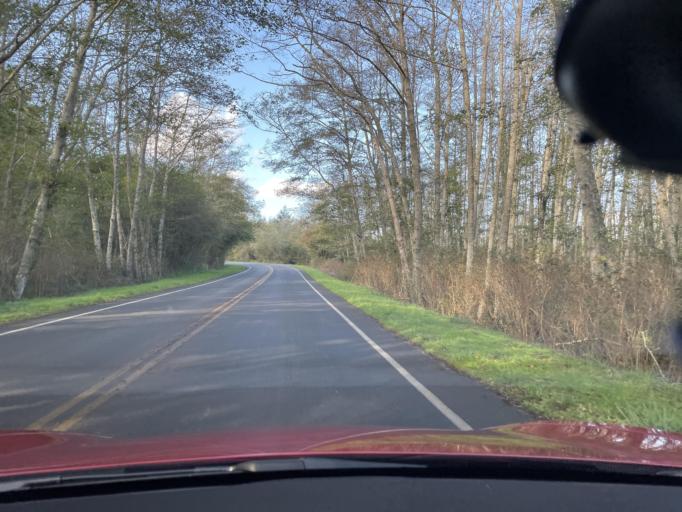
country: US
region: Washington
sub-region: San Juan County
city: Friday Harbor
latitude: 48.4669
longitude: -123.0066
